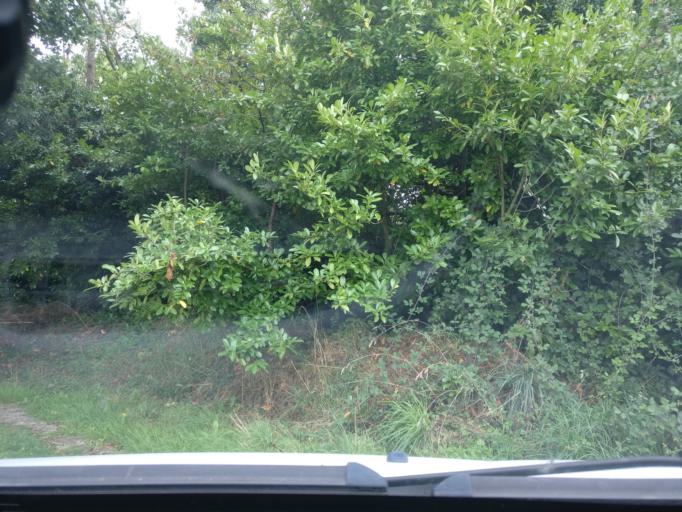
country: FR
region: Brittany
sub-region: Departement d'Ille-et-Vilaine
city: Noyal-sur-Vilaine
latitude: 48.0931
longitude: -1.5508
